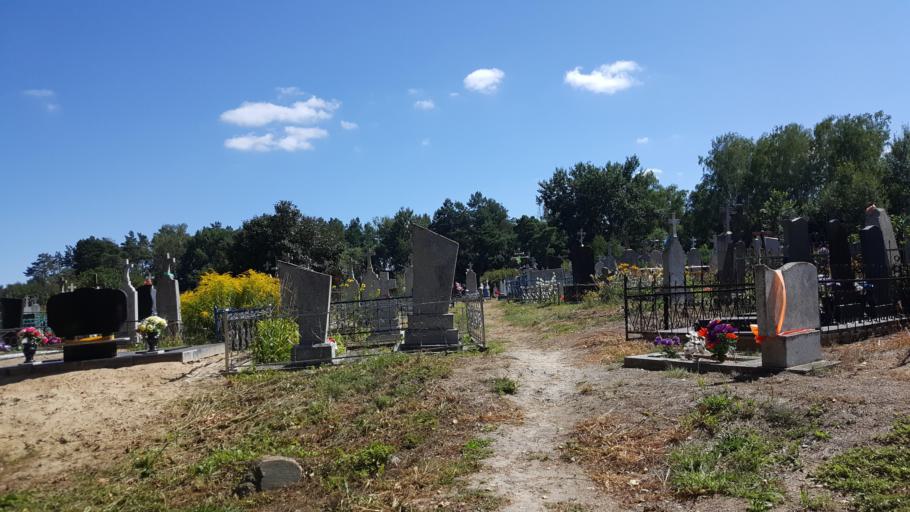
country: BY
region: Brest
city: Horad Kobryn
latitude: 52.2989
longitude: 24.3591
